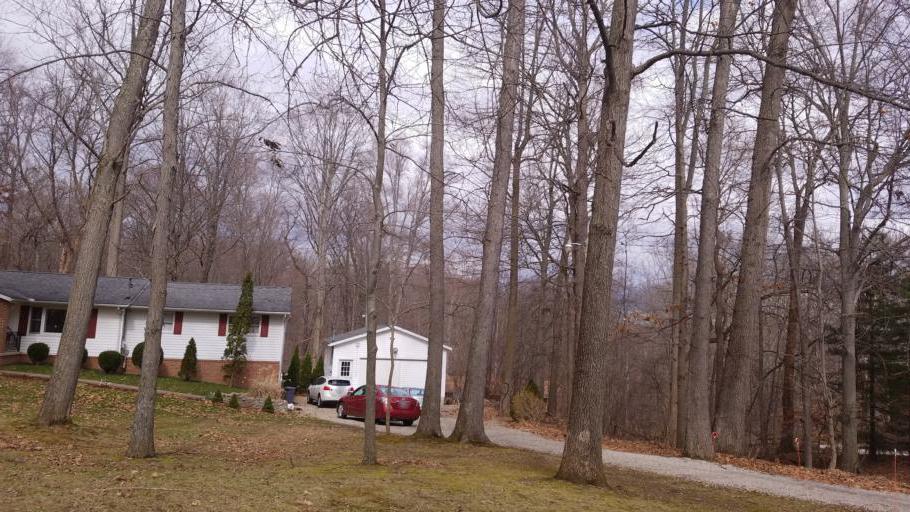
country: US
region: Ohio
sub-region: Muskingum County
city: Frazeysburg
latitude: 40.0609
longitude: -82.0904
